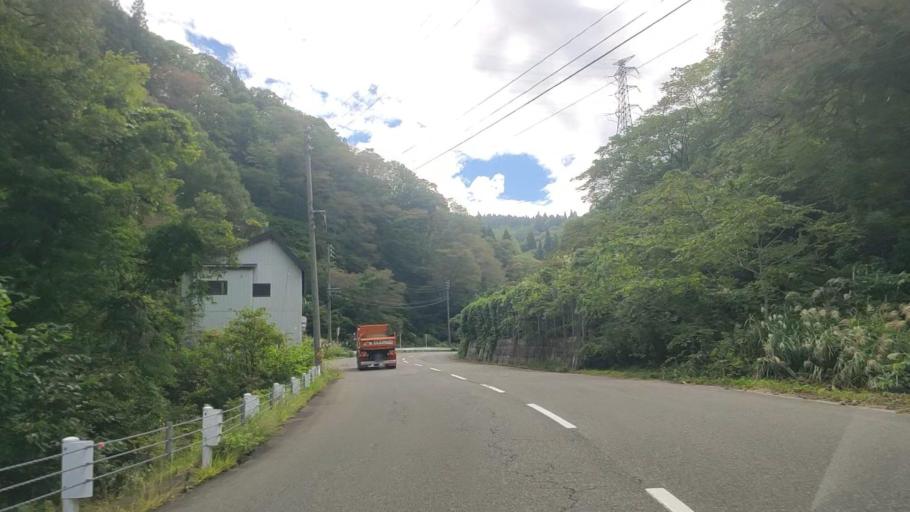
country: JP
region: Nagano
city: Iiyama
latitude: 36.8920
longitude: 138.3228
